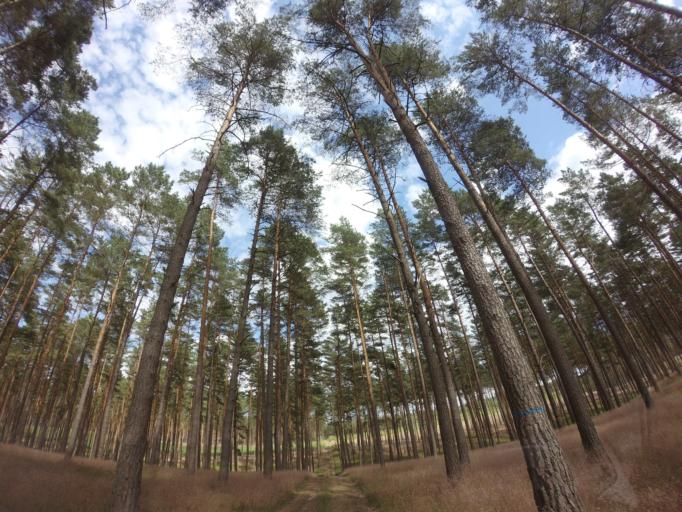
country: PL
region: West Pomeranian Voivodeship
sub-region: Powiat choszczenski
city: Drawno
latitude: 53.1549
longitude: 15.7290
